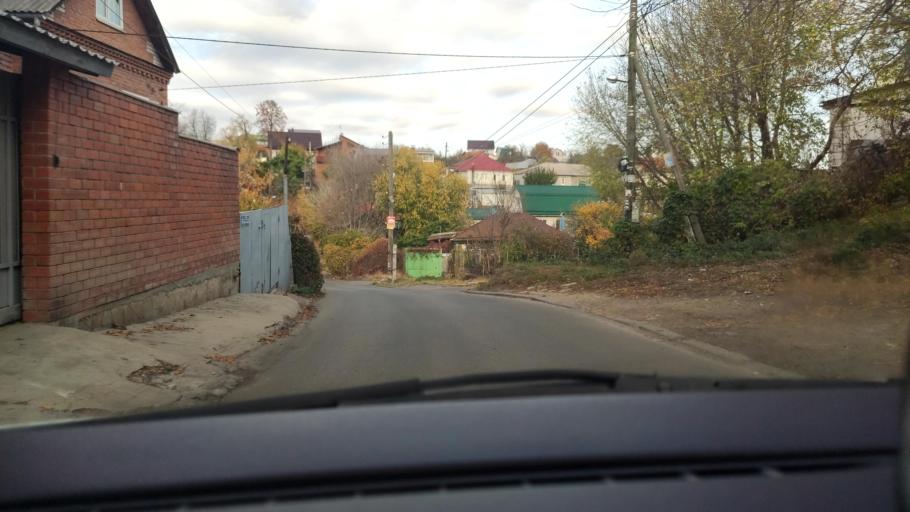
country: RU
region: Voronezj
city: Voronezh
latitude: 51.6851
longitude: 39.2247
